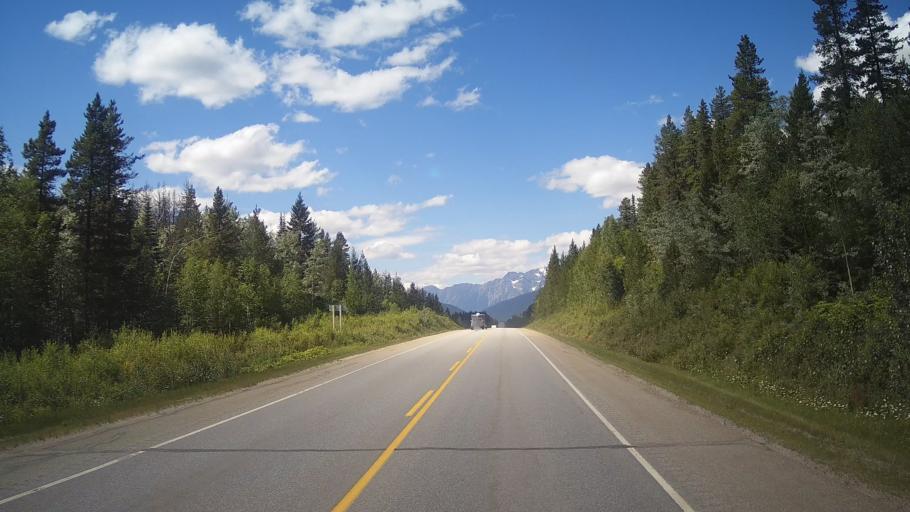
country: CA
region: Alberta
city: Jasper Park Lodge
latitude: 52.9756
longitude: -118.9615
